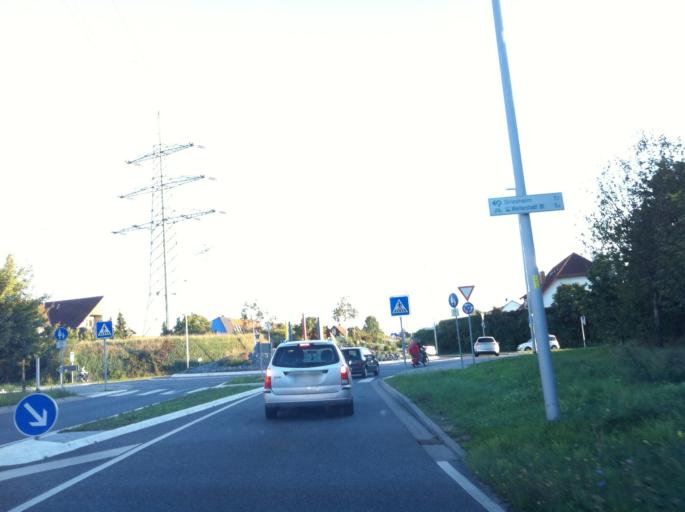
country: DE
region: Hesse
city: Weiterstadt
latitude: 49.9141
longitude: 8.5772
